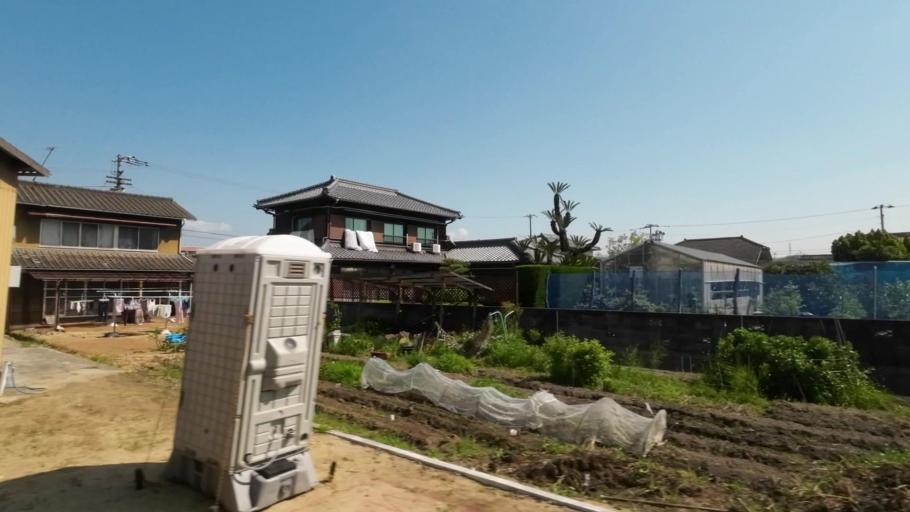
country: JP
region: Kagawa
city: Tadotsu
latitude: 34.2541
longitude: 133.7285
